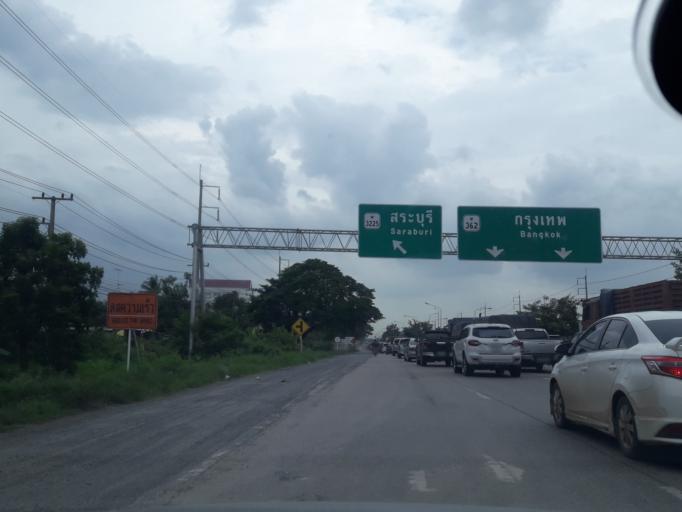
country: TH
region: Sara Buri
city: Saraburi
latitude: 14.5577
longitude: 100.9002
